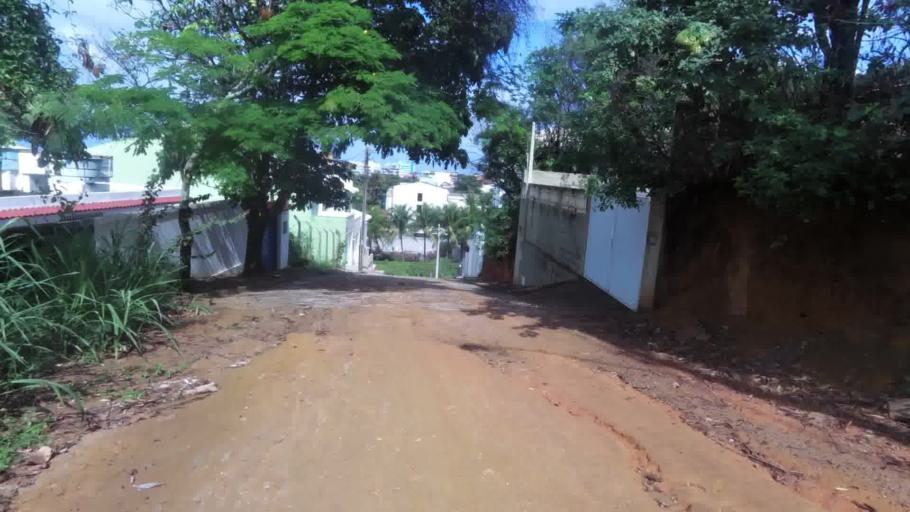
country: BR
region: Espirito Santo
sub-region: Piuma
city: Piuma
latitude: -20.8276
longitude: -40.6912
